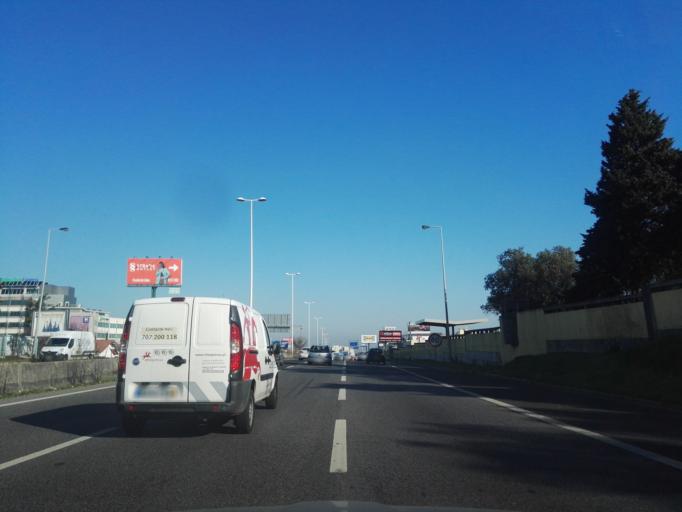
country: PT
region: Lisbon
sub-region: Loures
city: Sacavem
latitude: 38.7844
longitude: -9.1207
